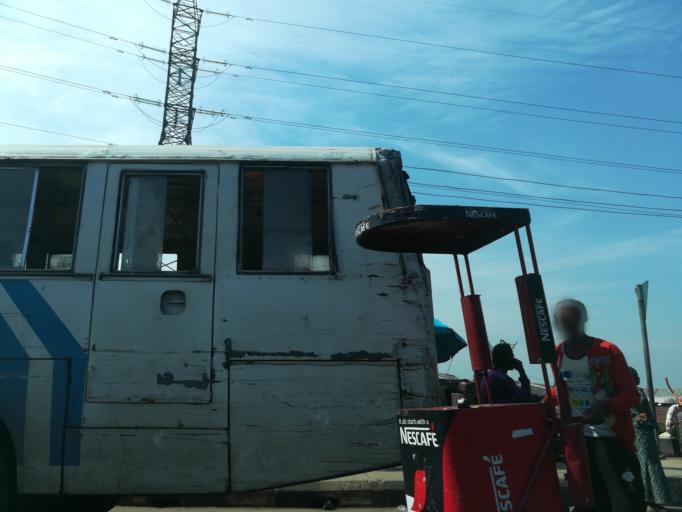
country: NG
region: Lagos
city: Ebute Ikorodu
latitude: 6.6193
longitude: 3.4744
